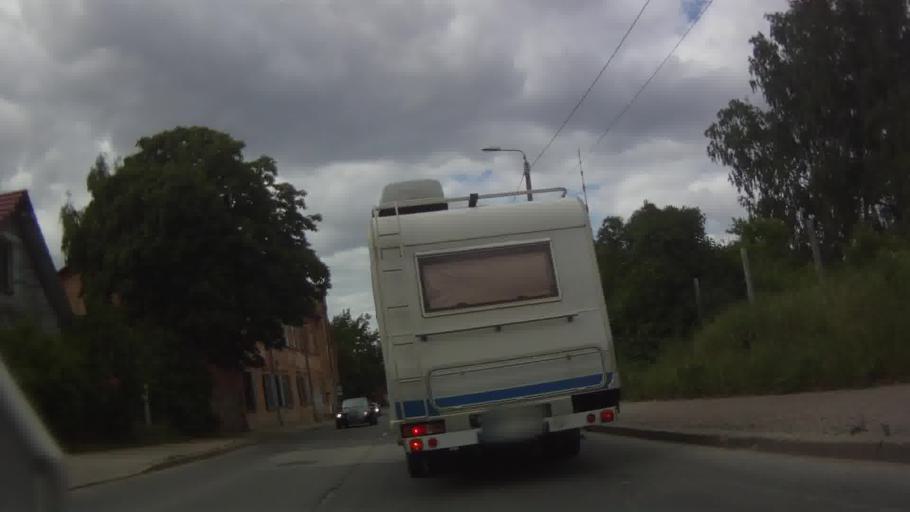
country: LV
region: Kekava
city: Balozi
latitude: 56.9135
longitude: 24.1422
